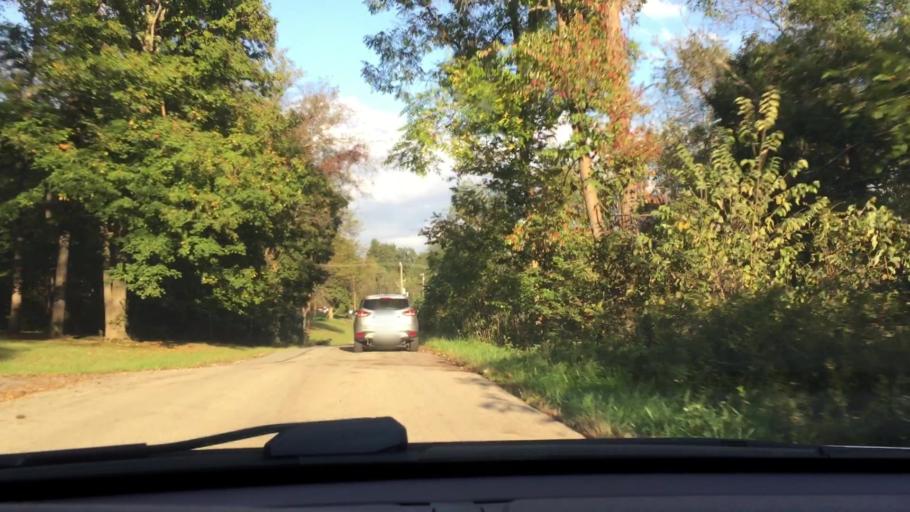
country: US
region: Pennsylvania
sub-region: Washington County
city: Bentleyville
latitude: 40.1314
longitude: -79.9769
